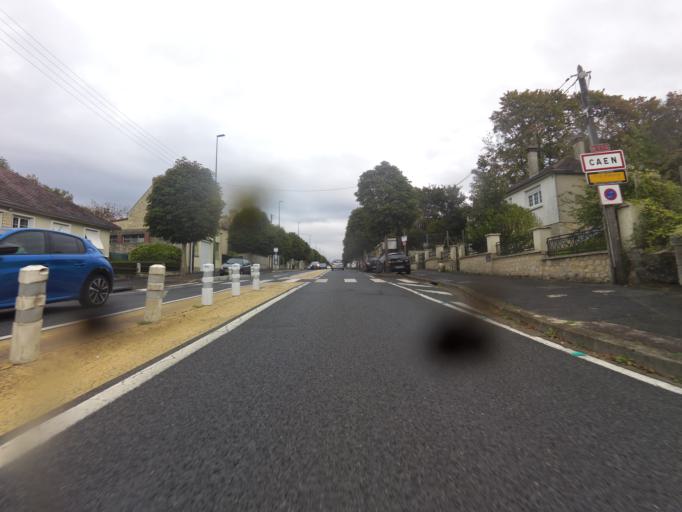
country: FR
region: Lower Normandy
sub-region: Departement du Calvados
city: Saint-Germain-la-Blanche-Herbe
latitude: 49.1698
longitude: -0.4035
